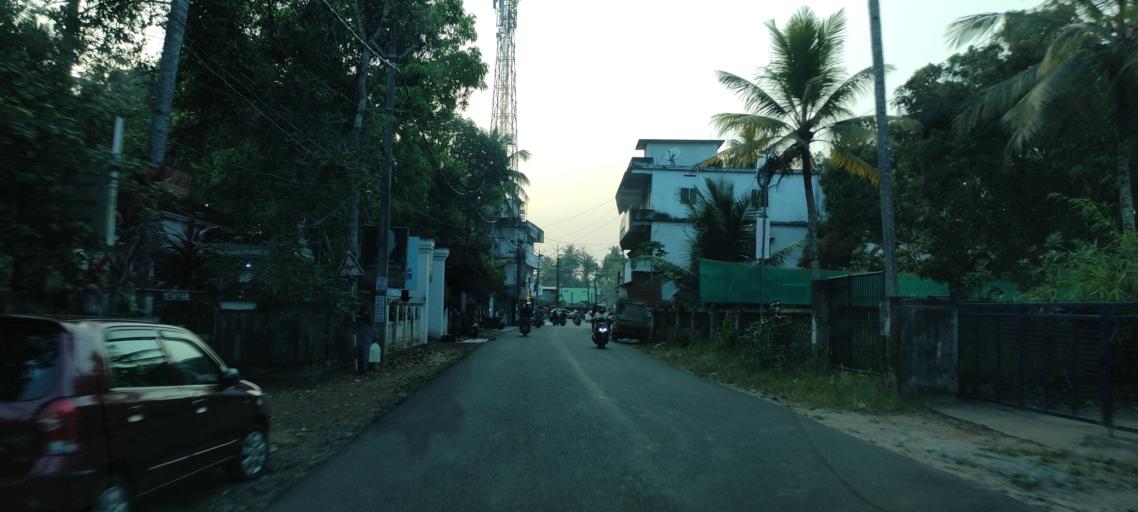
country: IN
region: Kerala
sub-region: Alappuzha
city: Kayankulam
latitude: 9.1375
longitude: 76.5135
